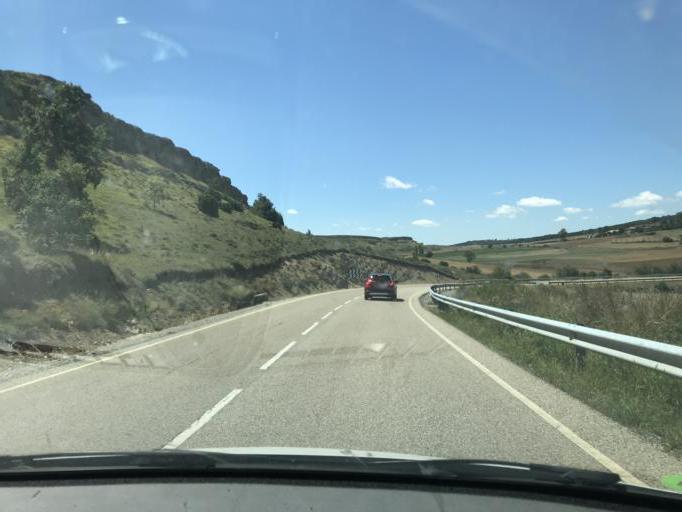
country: ES
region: Castille and Leon
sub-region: Provincia de Palencia
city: Dehesa de Montejo
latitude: 42.8236
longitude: -4.4972
